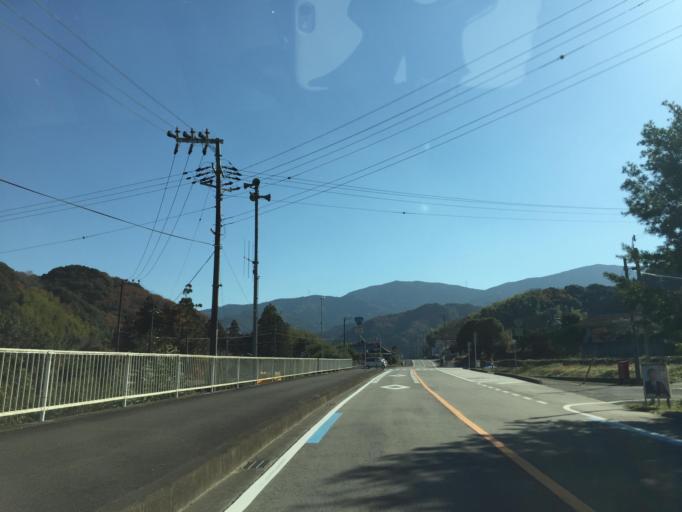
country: JP
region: Wakayama
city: Iwade
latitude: 34.1536
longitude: 135.3434
